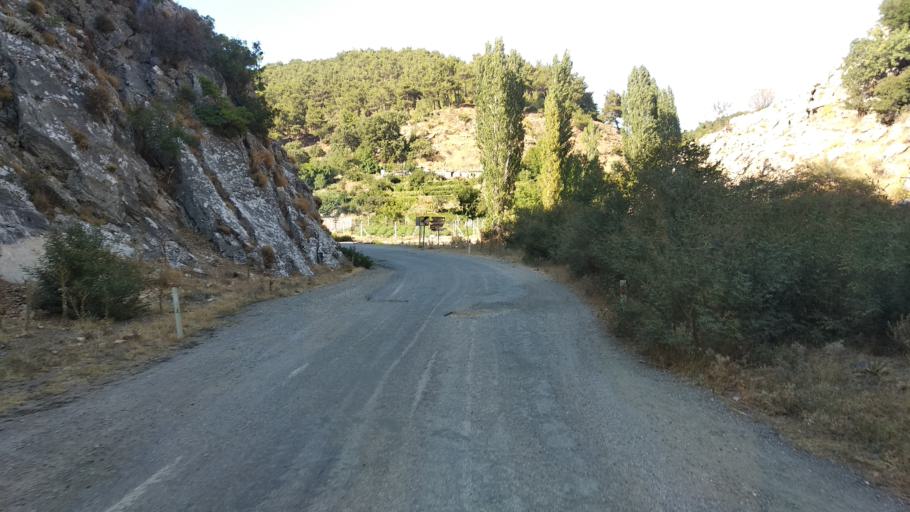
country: TR
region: Izmir
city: Gaziemir
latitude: 38.3235
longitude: 26.9573
